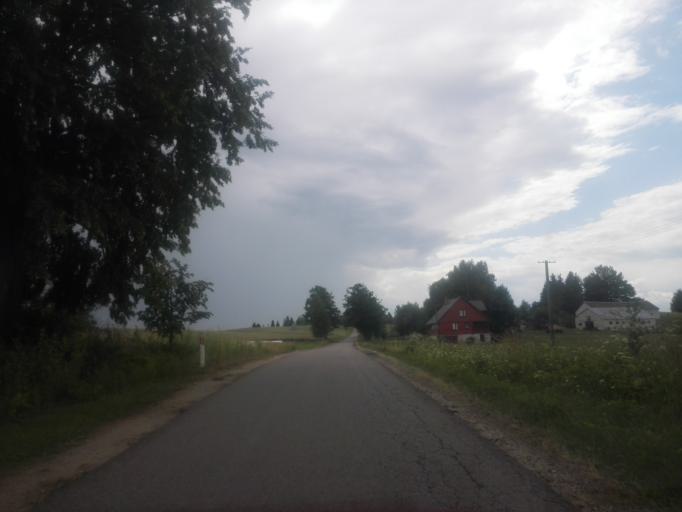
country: PL
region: Podlasie
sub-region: Powiat sejnenski
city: Sejny
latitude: 54.1435
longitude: 23.4223
